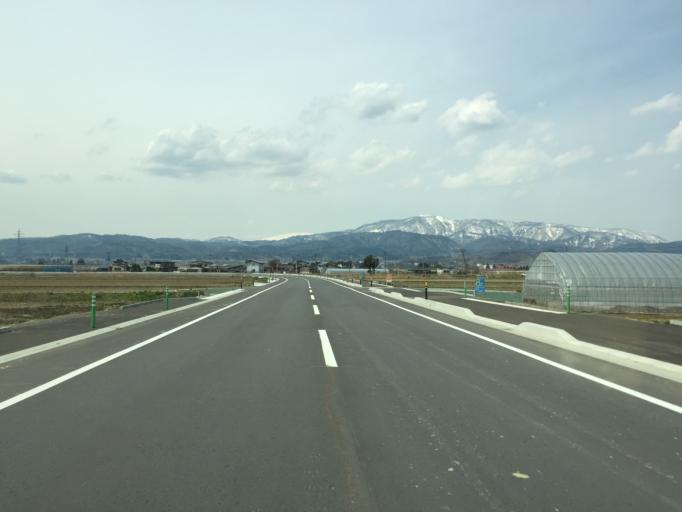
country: JP
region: Yamagata
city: Higashine
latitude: 38.4528
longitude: 140.3630
